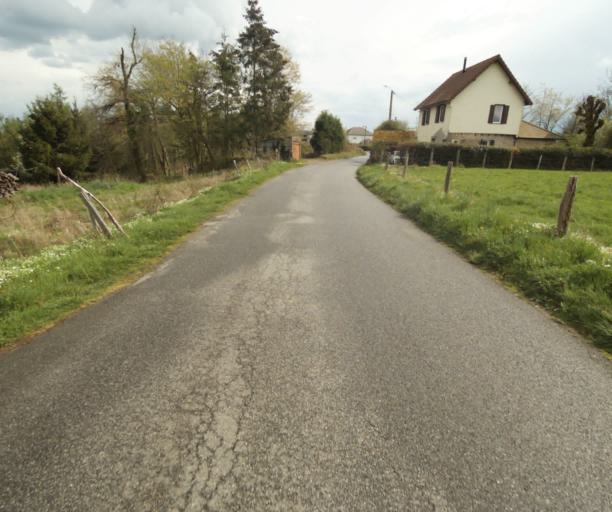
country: FR
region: Limousin
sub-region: Departement de la Correze
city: Tulle
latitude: 45.2787
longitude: 1.7489
